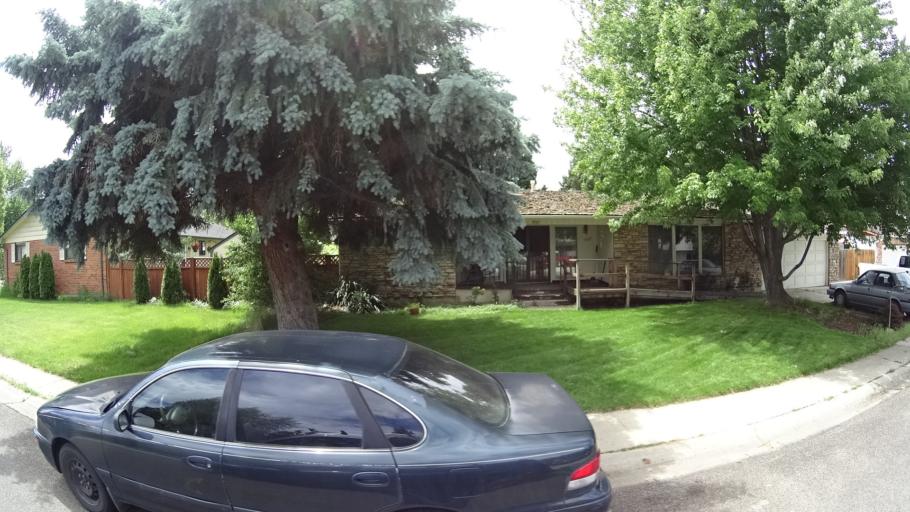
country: US
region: Idaho
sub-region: Ada County
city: Garden City
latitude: 43.6421
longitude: -116.2756
